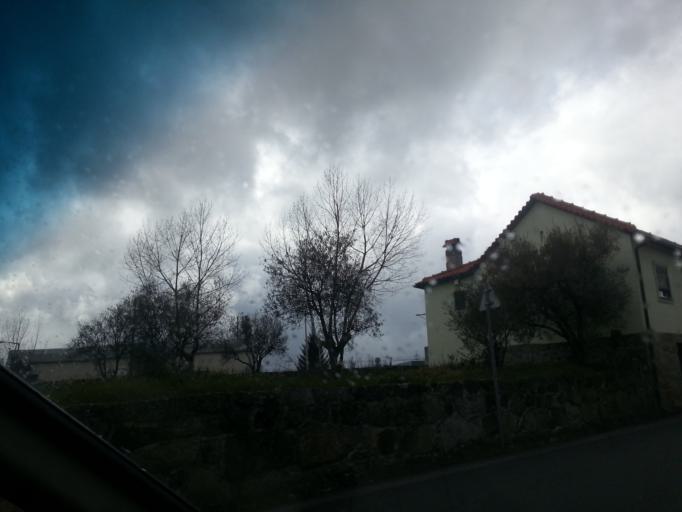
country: PT
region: Viseu
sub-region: Viseu
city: Rio de Loba
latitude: 40.6299
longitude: -7.8644
